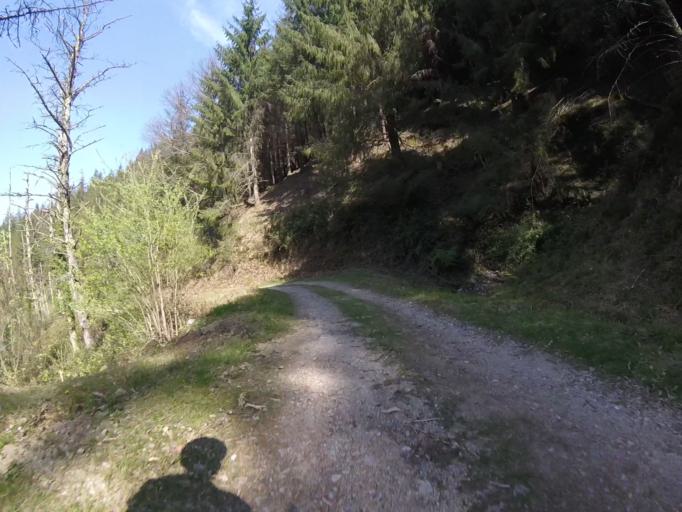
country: ES
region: Basque Country
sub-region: Provincia de Guipuzcoa
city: Irun
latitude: 43.2546
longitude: -1.8050
